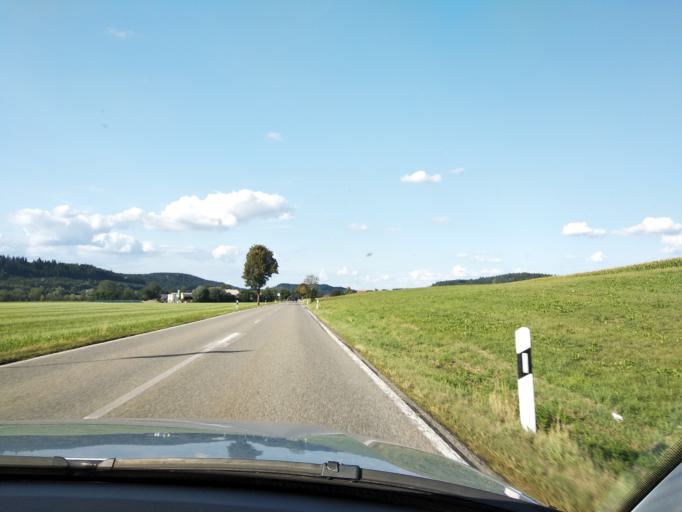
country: DE
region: Baden-Wuerttemberg
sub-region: Tuebingen Region
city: Leutkirch im Allgau
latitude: 47.8646
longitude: 10.0333
